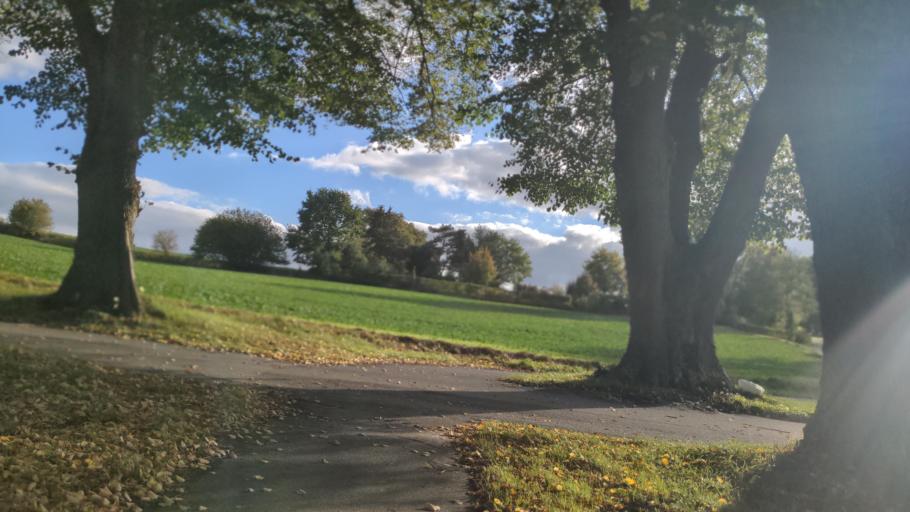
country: DE
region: Schleswig-Holstein
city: Bosau
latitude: 54.1206
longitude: 10.4451
